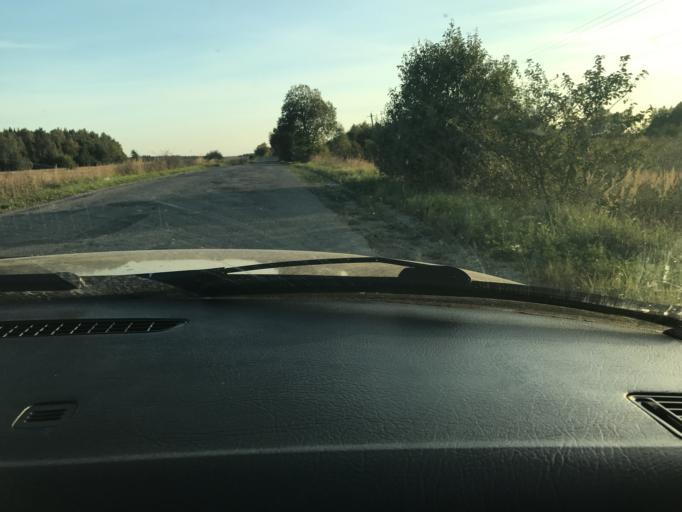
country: RU
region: Kaluga
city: Myatlevo
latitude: 54.7904
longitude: 35.7357
